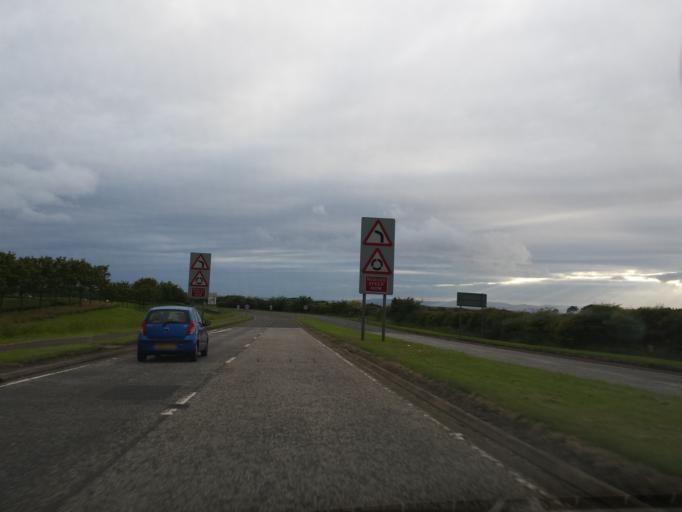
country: GB
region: Scotland
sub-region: South Ayrshire
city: Prestwick
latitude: 55.5216
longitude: -4.6138
